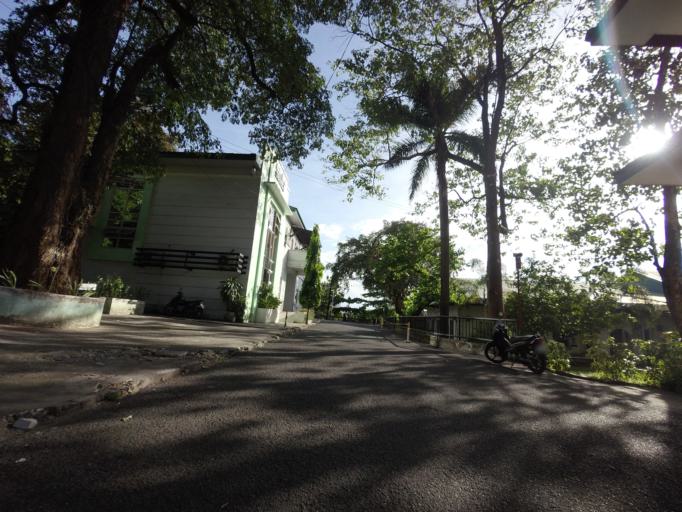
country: PH
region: Metro Manila
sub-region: Mandaluyong
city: Mandaluyong City
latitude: 14.5802
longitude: 121.0421
